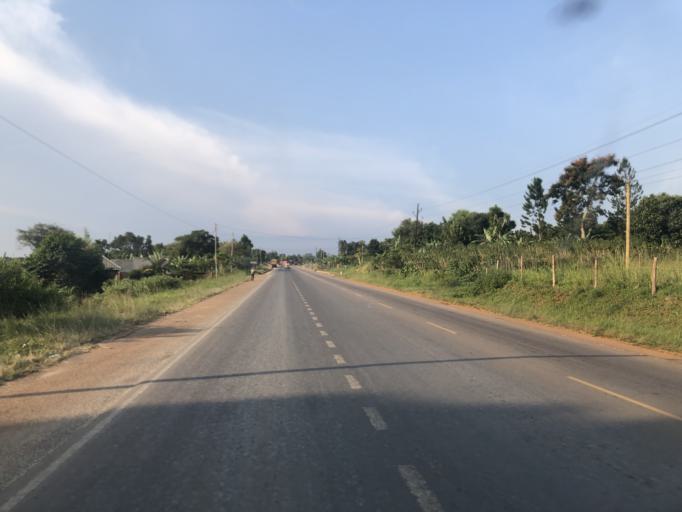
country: UG
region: Central Region
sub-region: Mpigi District
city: Mpigi
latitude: 0.1682
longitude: 32.2588
